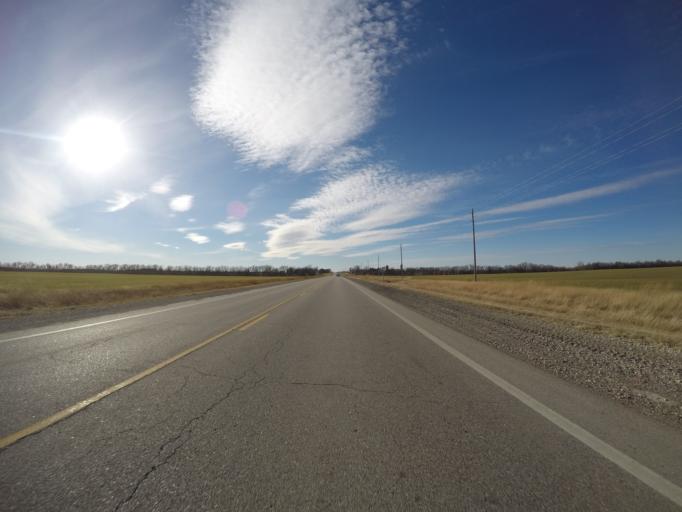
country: US
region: Kansas
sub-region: McPherson County
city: McPherson
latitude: 38.3771
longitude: -97.5053
